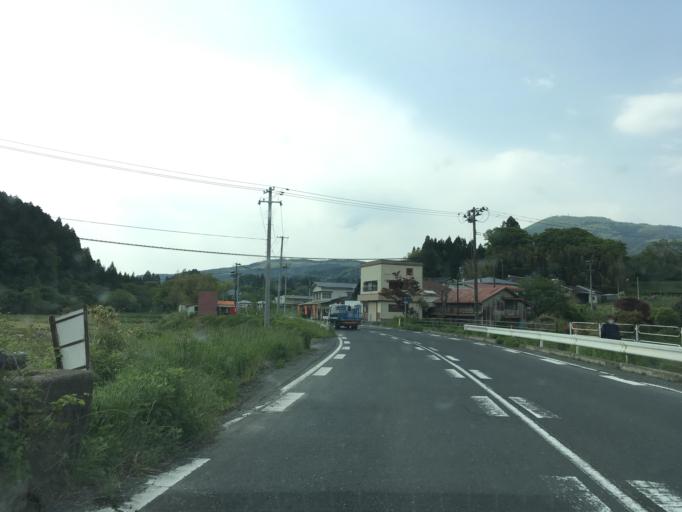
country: JP
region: Iwate
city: Ofunato
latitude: 38.9367
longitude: 141.4623
